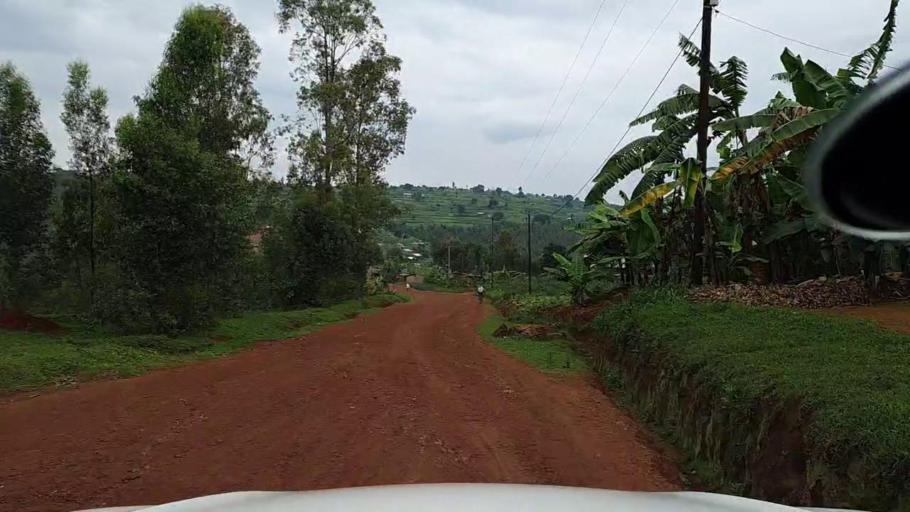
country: RW
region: Kigali
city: Kigali
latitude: -1.9076
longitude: 29.8985
